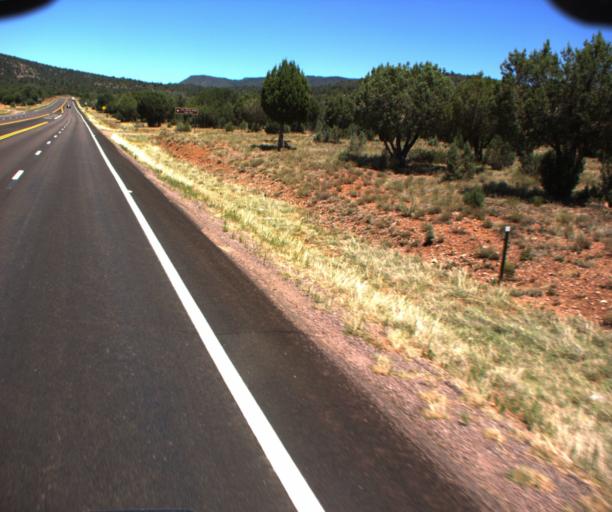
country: US
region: Arizona
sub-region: Gila County
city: Pine
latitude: 34.3331
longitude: -111.4199
